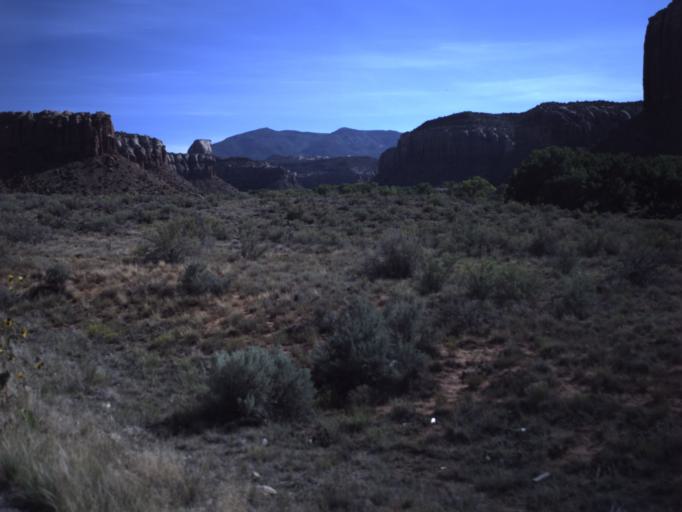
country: US
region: Utah
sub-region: San Juan County
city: Monticello
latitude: 38.0684
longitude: -109.5555
